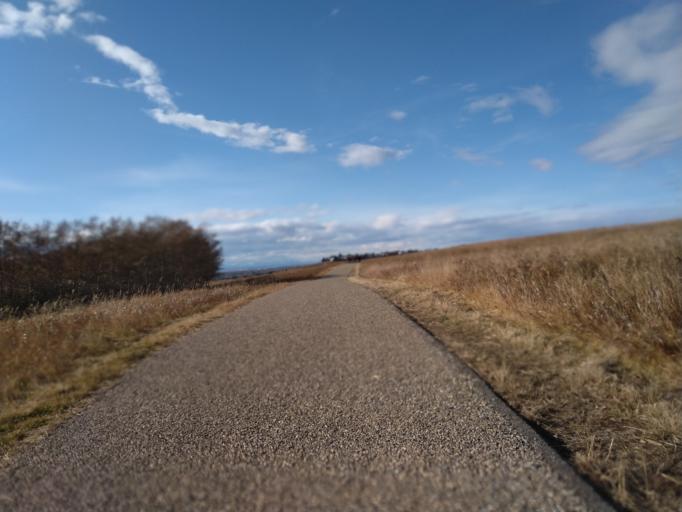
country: CA
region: Alberta
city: Calgary
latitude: 51.1109
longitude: -114.1228
